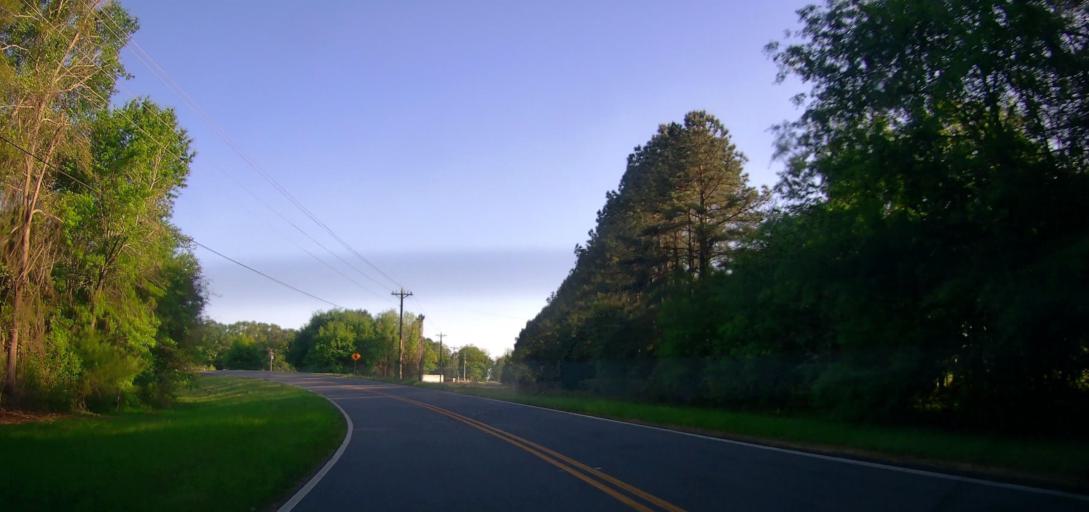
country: US
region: Georgia
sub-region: Macon County
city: Oglethorpe
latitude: 32.2705
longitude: -84.0853
